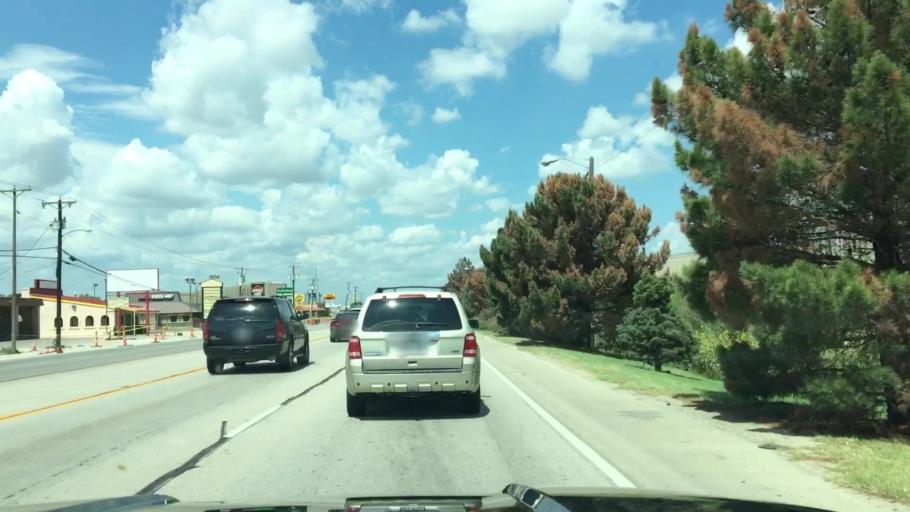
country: US
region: Texas
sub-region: Tarrant County
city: Saginaw
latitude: 32.8510
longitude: -97.3604
